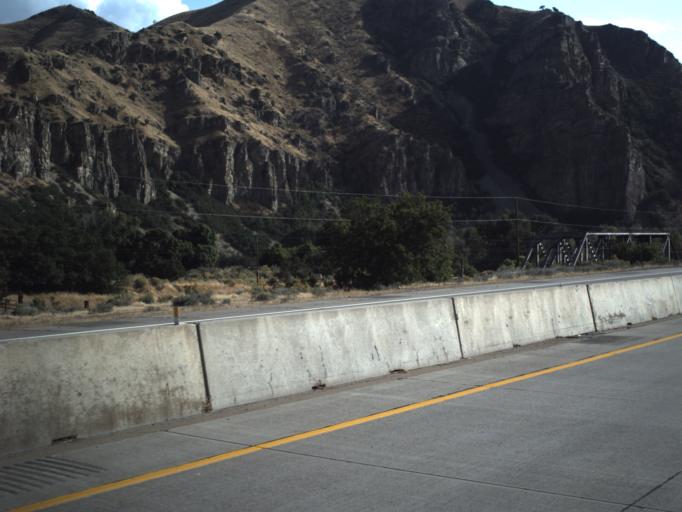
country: US
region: Utah
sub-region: Morgan County
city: Morgan
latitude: 41.0513
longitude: -111.6038
